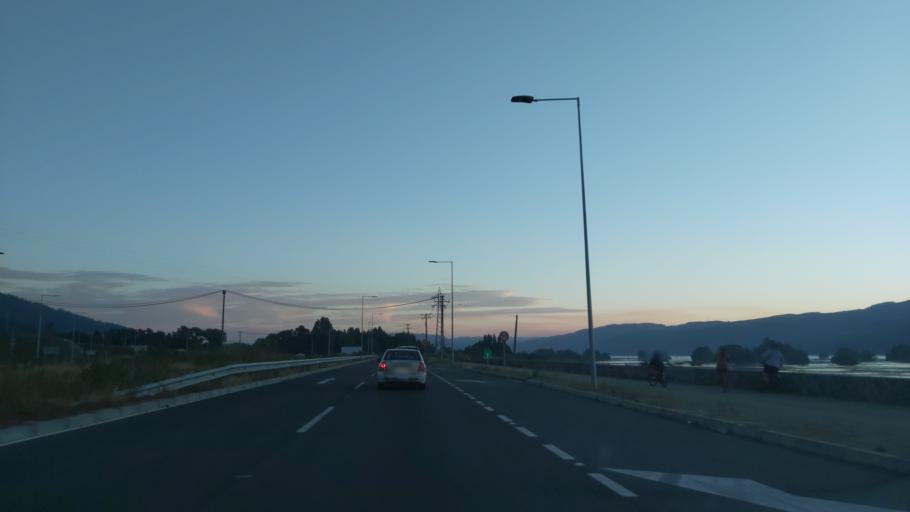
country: CL
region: Biobio
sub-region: Provincia de Concepcion
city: Chiguayante
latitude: -36.8920
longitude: -73.0367
